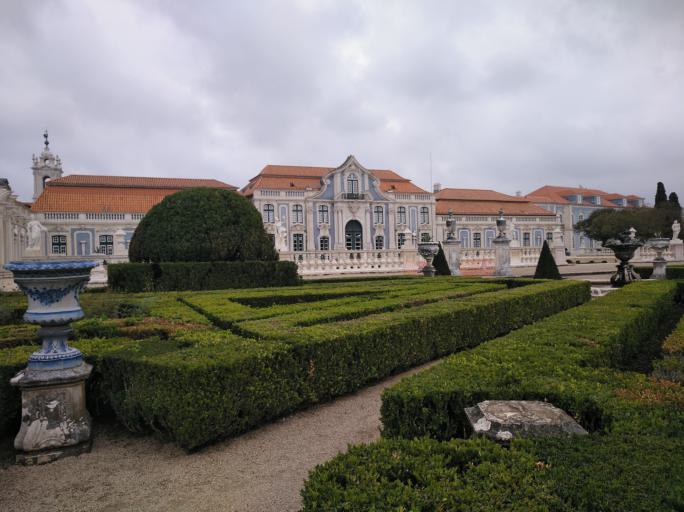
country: PT
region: Lisbon
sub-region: Sintra
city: Queluz
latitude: 38.7502
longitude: -9.2590
